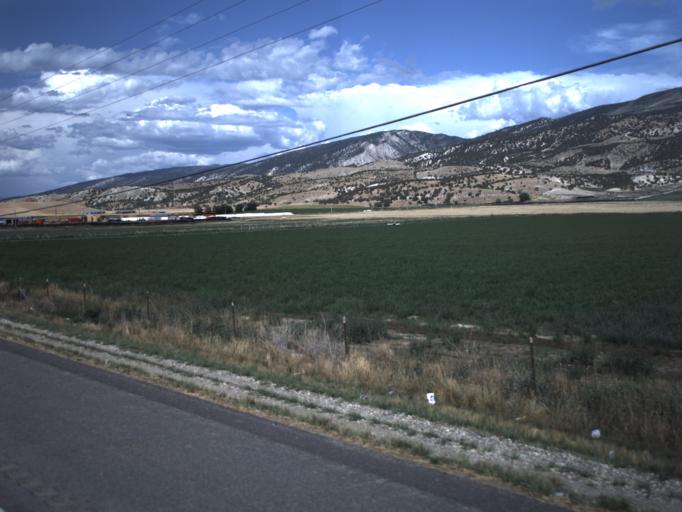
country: US
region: Utah
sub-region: Sanpete County
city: Manti
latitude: 39.2891
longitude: -111.6251
